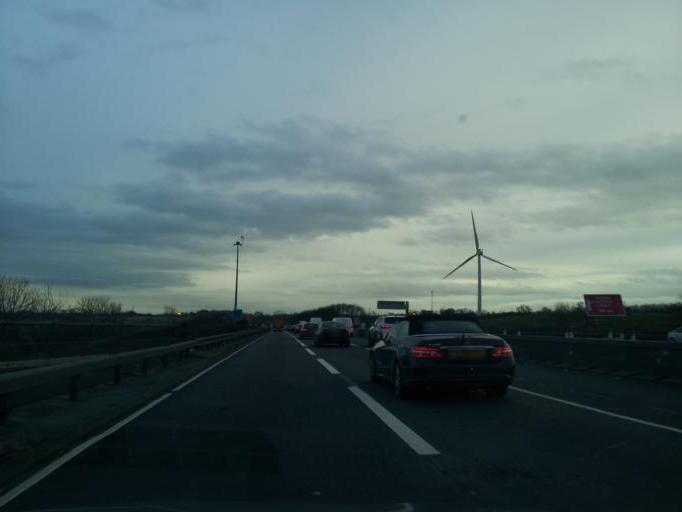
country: GB
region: England
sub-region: Northamptonshire
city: Long Buckby
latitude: 52.3514
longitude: -1.1544
